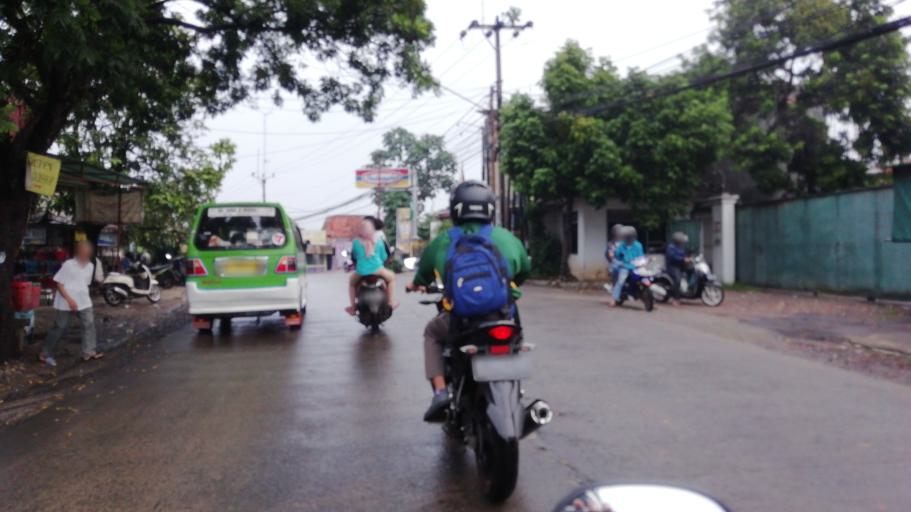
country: ID
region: West Java
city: Bogor
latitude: -6.5520
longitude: 106.8073
